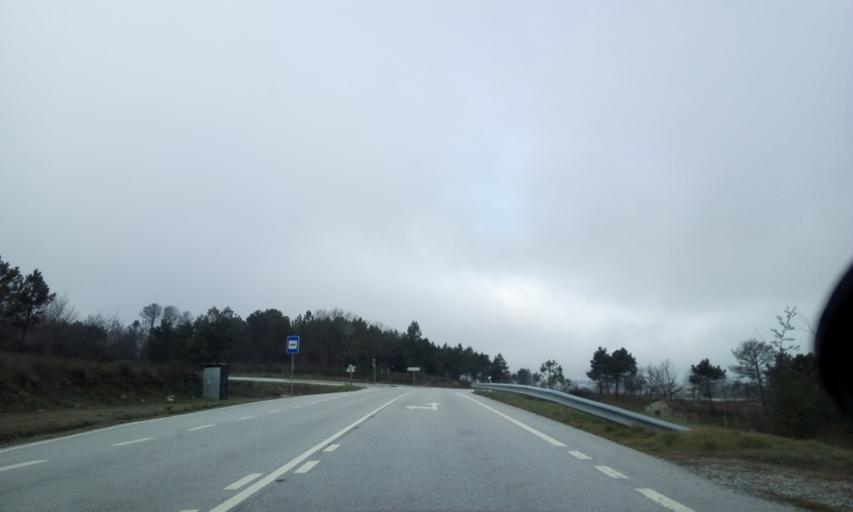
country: PT
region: Guarda
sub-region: Fornos de Algodres
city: Fornos de Algodres
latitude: 40.6919
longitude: -7.4700
